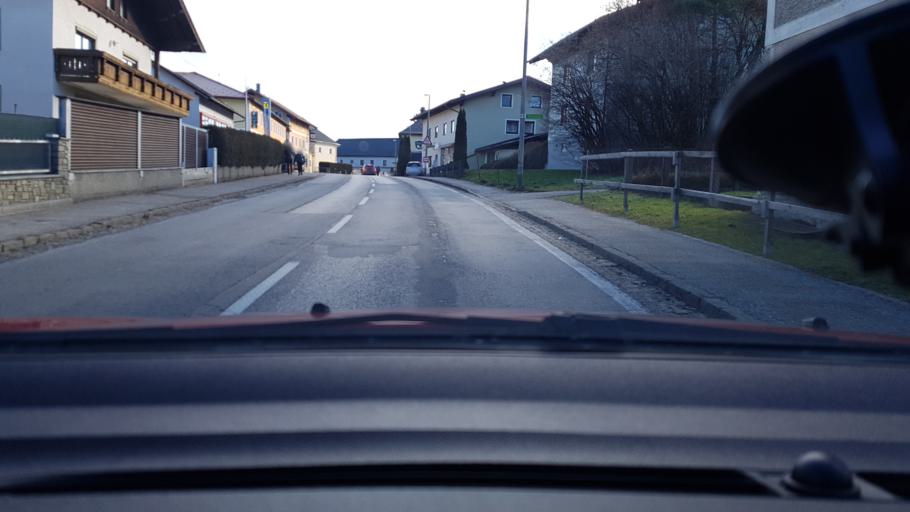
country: AT
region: Salzburg
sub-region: Politischer Bezirk Salzburg-Umgebung
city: Dorfbeuern
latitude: 48.0465
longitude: 12.9884
